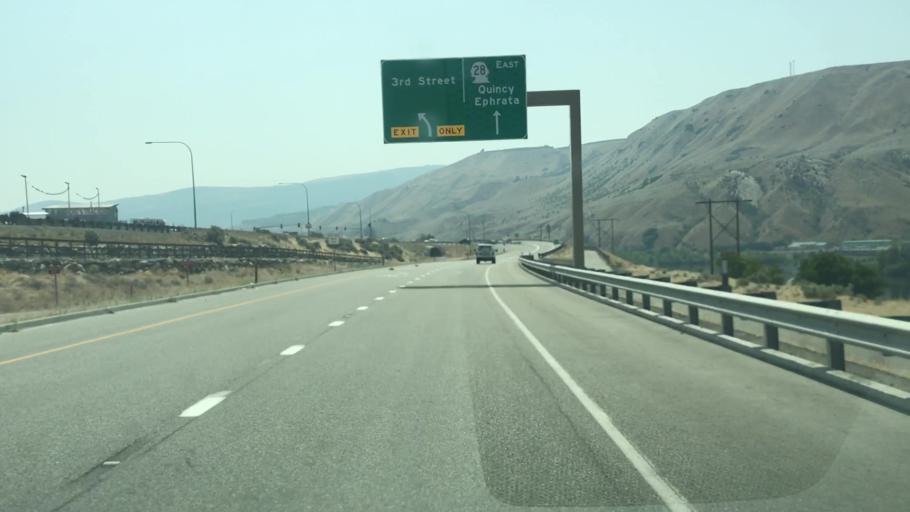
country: US
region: Washington
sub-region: Chelan County
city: South Wenatchee
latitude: 47.4017
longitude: -120.2895
